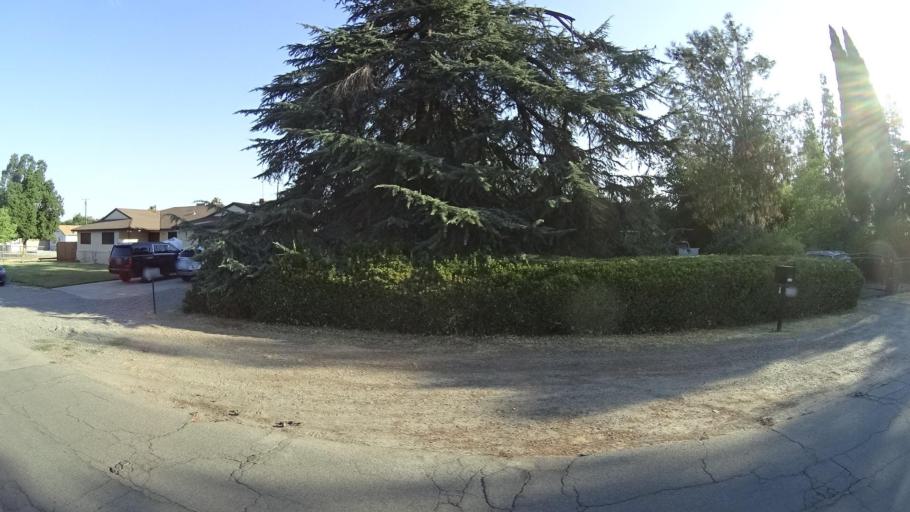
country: US
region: California
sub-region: Fresno County
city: Sunnyside
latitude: 36.7371
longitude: -119.7062
